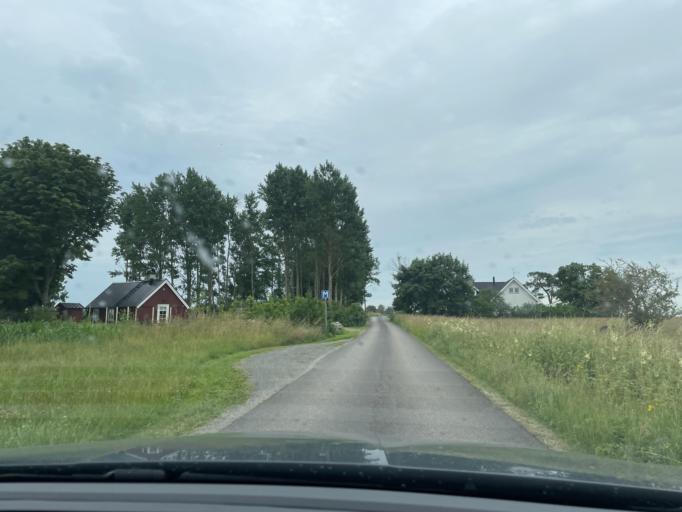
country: SE
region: Skane
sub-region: Bromolla Kommun
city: Bromoella
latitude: 56.0052
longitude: 14.4388
